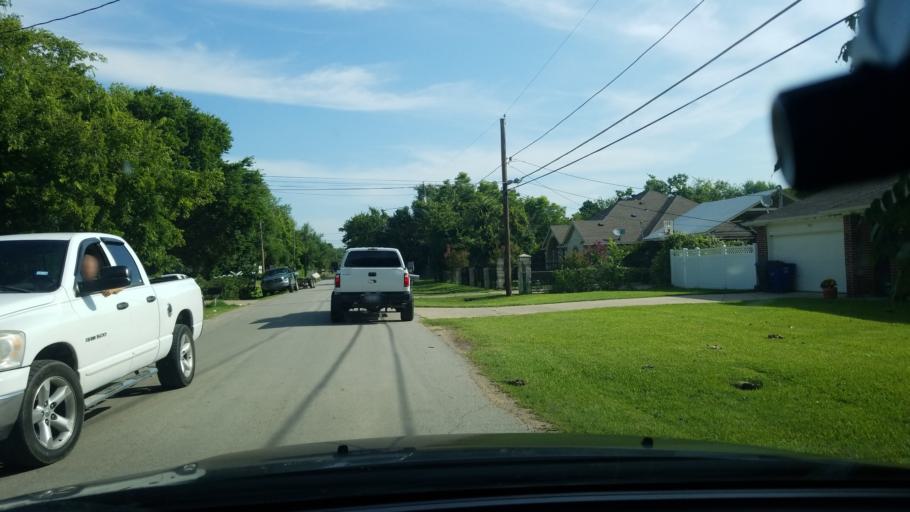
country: US
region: Texas
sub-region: Dallas County
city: Balch Springs
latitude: 32.7151
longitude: -96.6388
